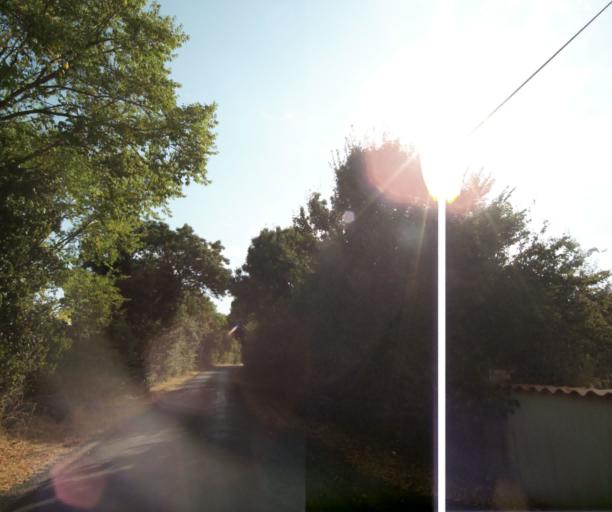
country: FR
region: Poitou-Charentes
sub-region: Departement de la Charente-Maritime
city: Tonnay-Charente
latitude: 45.9662
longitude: -0.8675
